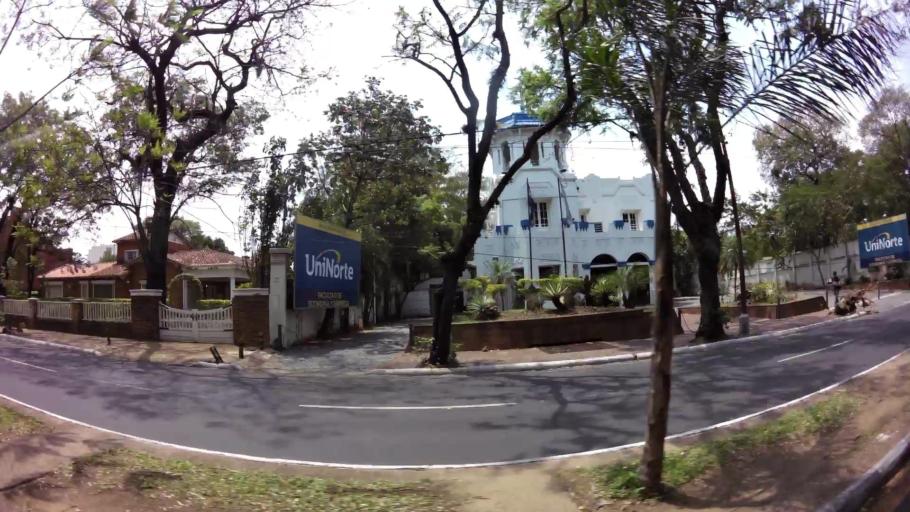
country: PY
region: Asuncion
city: Asuncion
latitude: -25.2936
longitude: -57.6119
